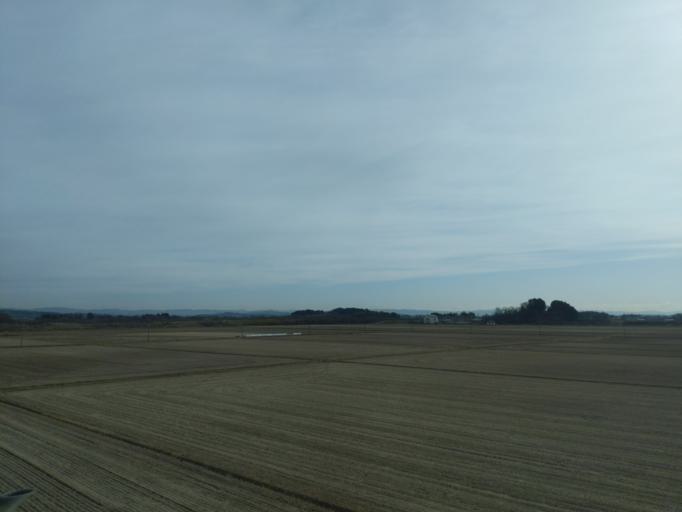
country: JP
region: Iwate
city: Ichinoseki
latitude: 38.7824
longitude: 141.0906
